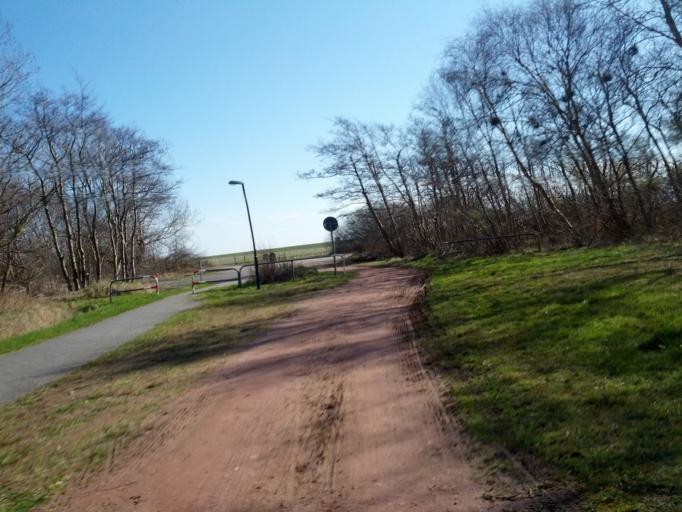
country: DE
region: Lower Saxony
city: Langeoog
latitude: 53.7337
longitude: 7.4833
